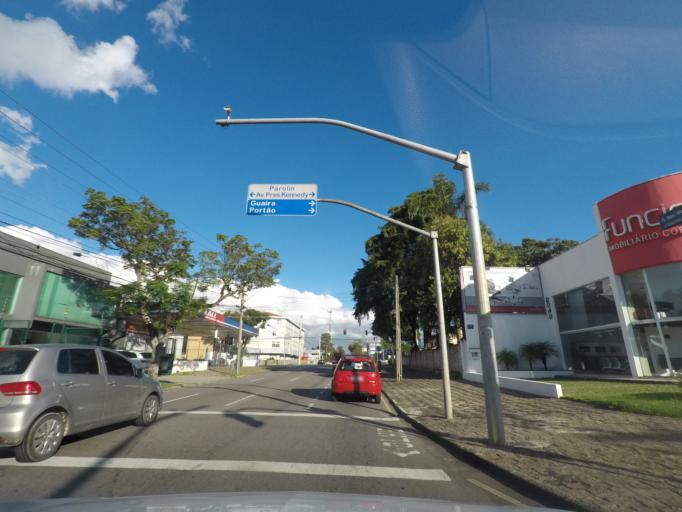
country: BR
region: Parana
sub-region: Curitiba
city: Curitiba
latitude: -25.4515
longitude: -49.2642
